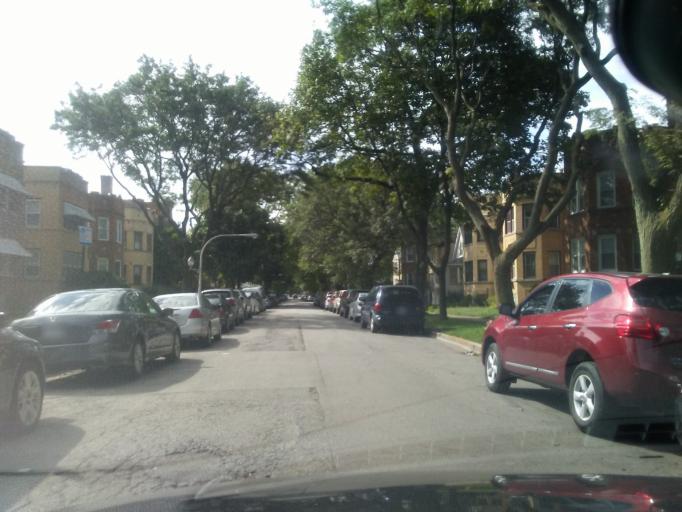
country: US
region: Illinois
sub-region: Cook County
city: Lincolnwood
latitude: 41.9933
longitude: -87.6922
